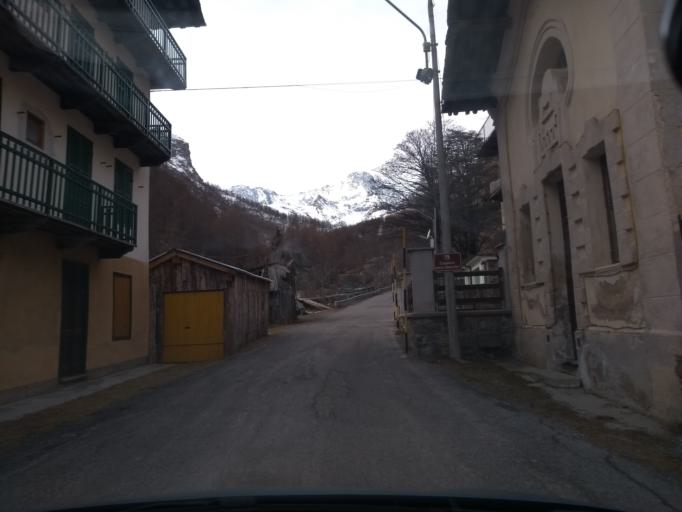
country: IT
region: Piedmont
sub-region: Provincia di Torino
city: Balme
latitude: 45.3026
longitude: 7.2134
